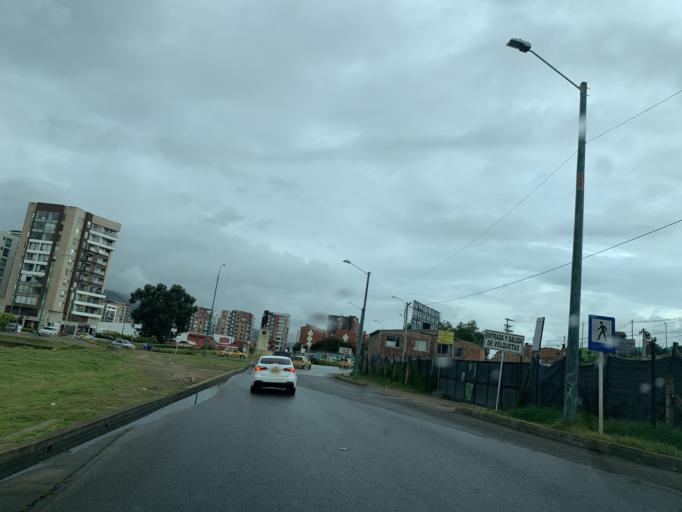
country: CO
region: Boyaca
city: Tunja
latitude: 5.5408
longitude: -73.3505
